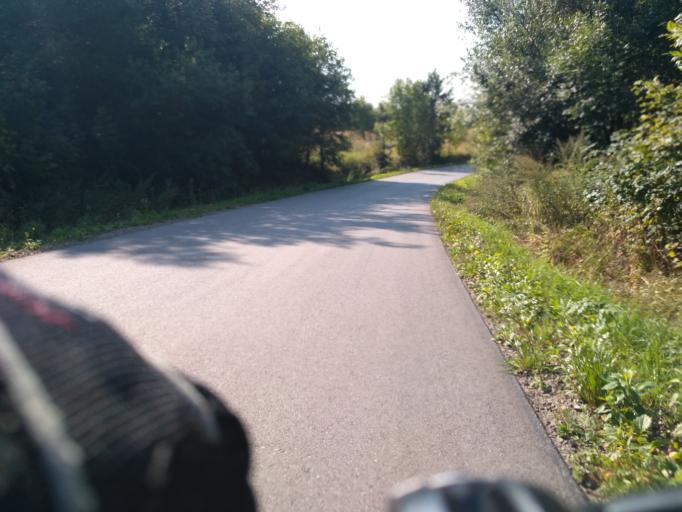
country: PL
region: Subcarpathian Voivodeship
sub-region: Powiat brzozowski
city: Golcowa
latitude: 49.8049
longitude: 22.0249
